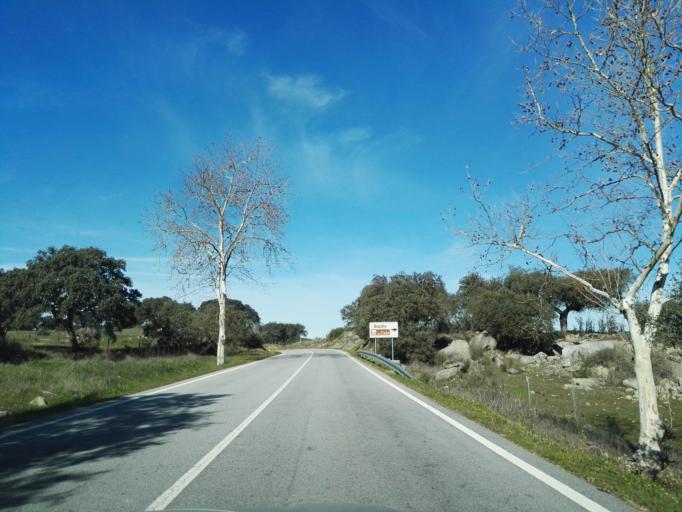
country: PT
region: Portalegre
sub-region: Arronches
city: Arronches
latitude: 39.0624
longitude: -7.2737
